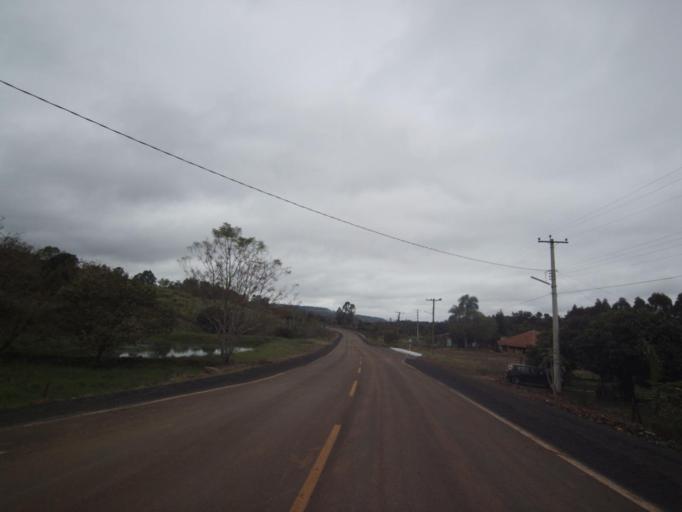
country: AR
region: Misiones
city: El Soberbio
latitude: -27.2905
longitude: -54.1900
